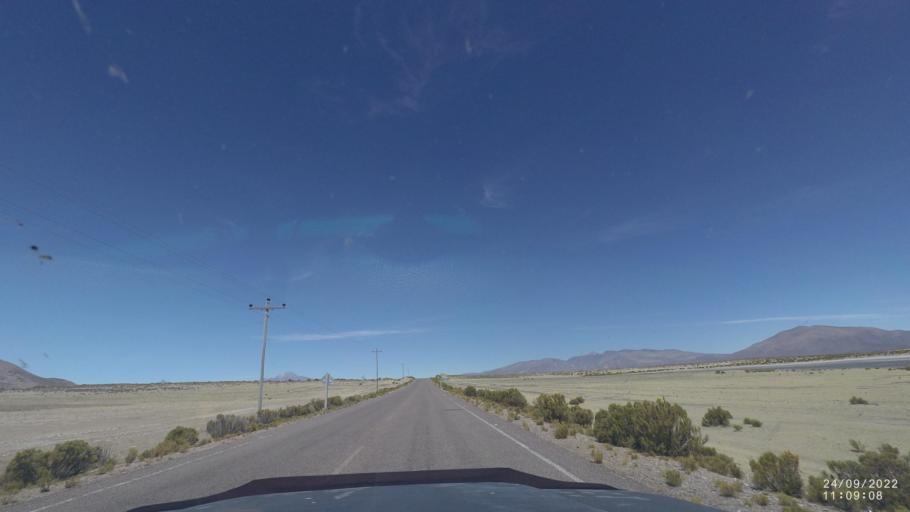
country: BO
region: Oruro
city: Challapata
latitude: -19.4919
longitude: -67.4473
